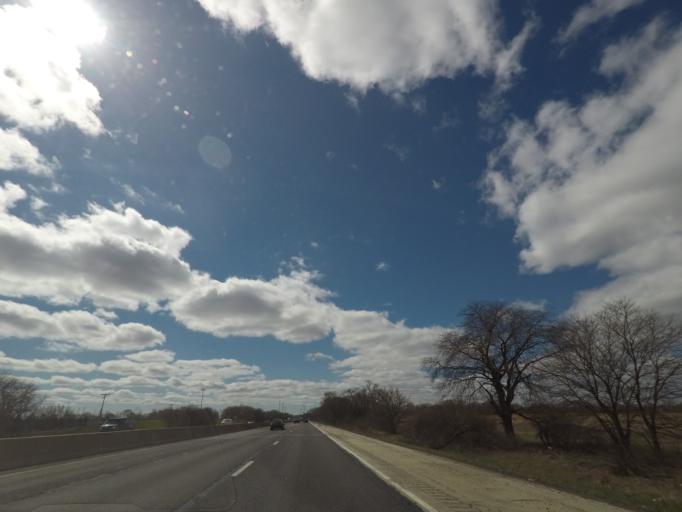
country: US
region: Illinois
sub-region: Will County
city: Crystal Lawns
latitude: 41.5999
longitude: -88.1633
